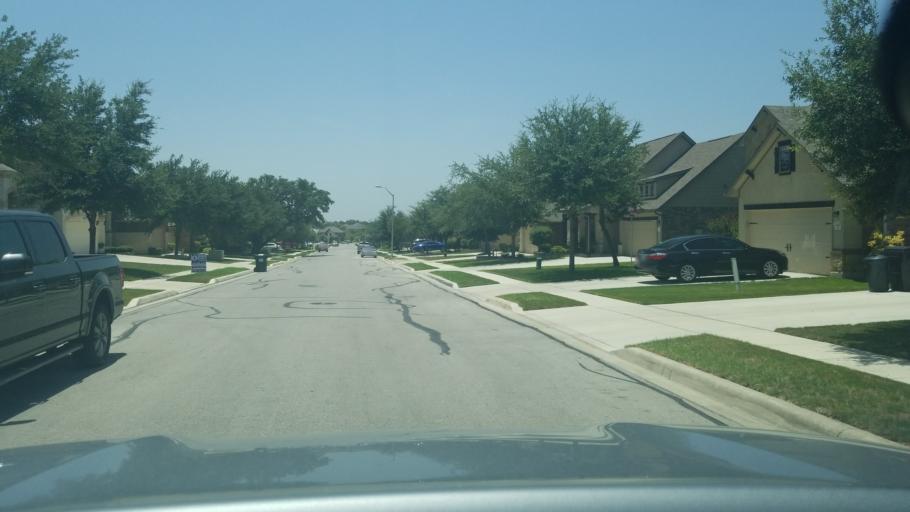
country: US
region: Texas
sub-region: Guadalupe County
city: Cibolo
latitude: 29.5802
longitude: -98.2282
